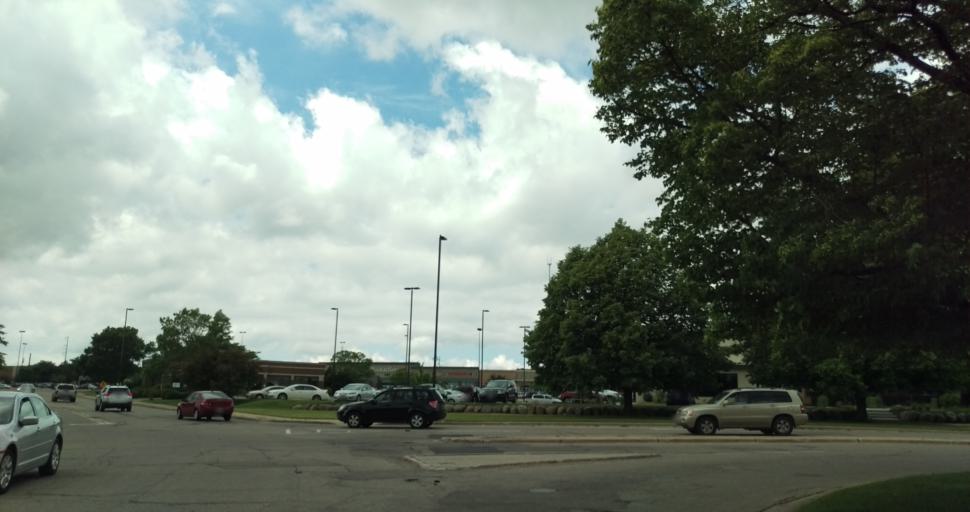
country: US
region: Wisconsin
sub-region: Dane County
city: Middleton
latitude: 43.0600
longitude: -89.5075
